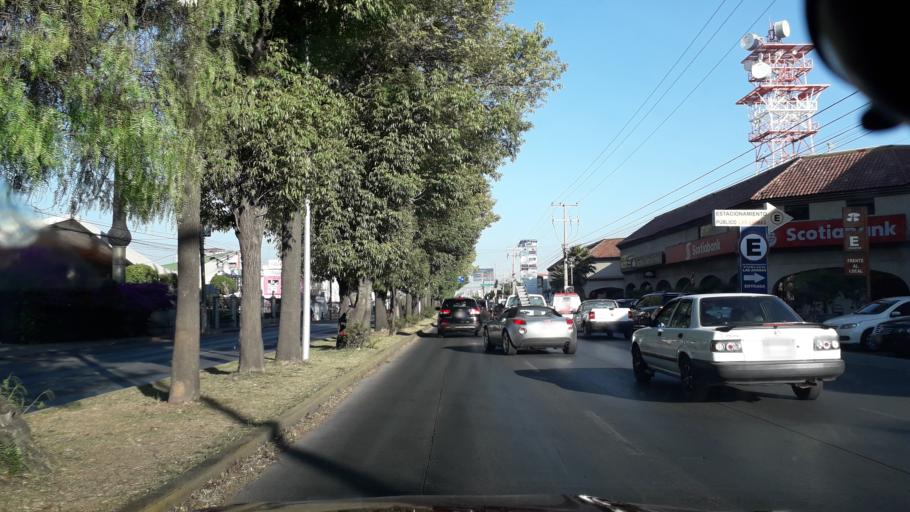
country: MX
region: Puebla
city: Puebla
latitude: 19.0423
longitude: -98.2314
